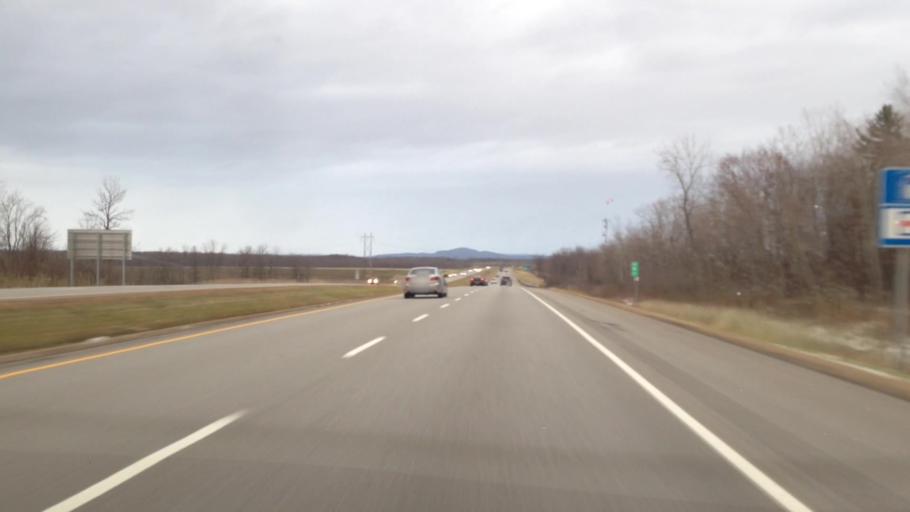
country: CA
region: Quebec
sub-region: Monteregie
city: Rigaud
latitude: 45.4862
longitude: -74.3316
